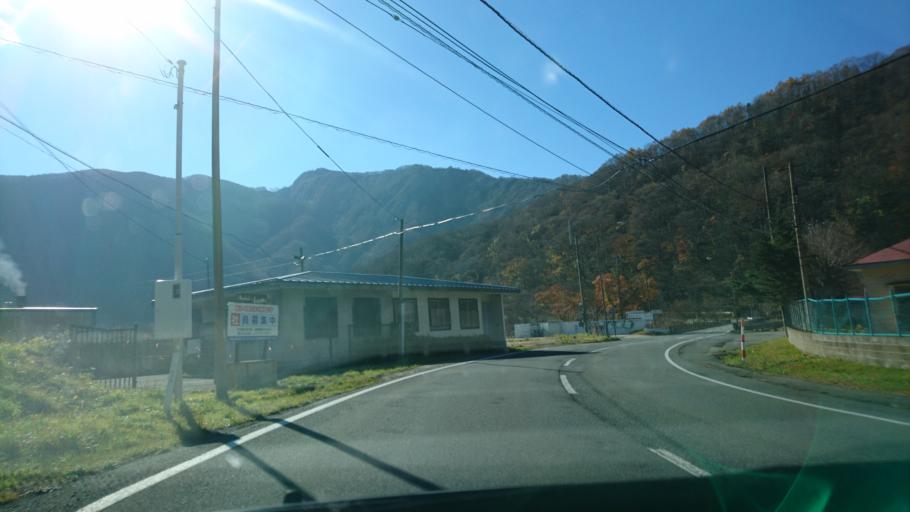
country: JP
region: Iwate
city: Kitakami
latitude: 39.3050
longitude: 140.9023
